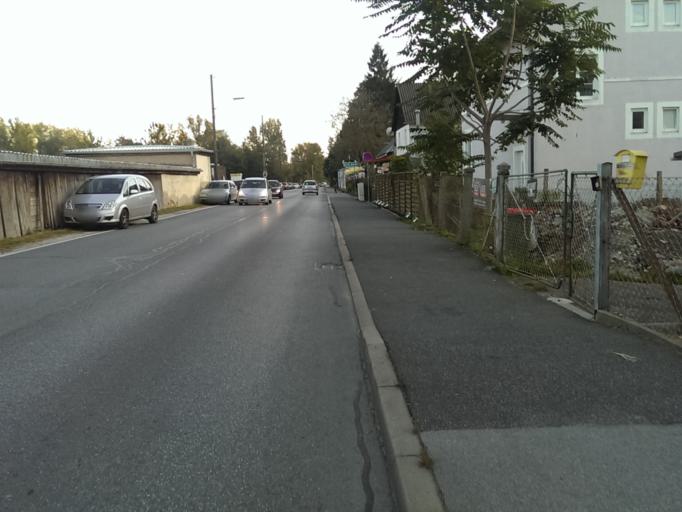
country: AT
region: Styria
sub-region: Graz Stadt
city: Goesting
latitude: 47.0920
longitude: 15.4015
